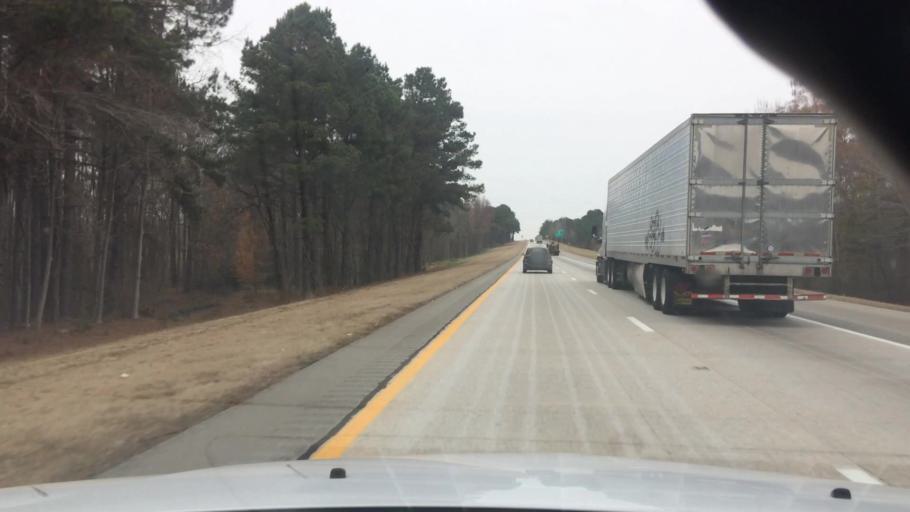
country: US
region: North Carolina
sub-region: Nash County
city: Nashville
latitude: 35.9543
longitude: -77.8884
